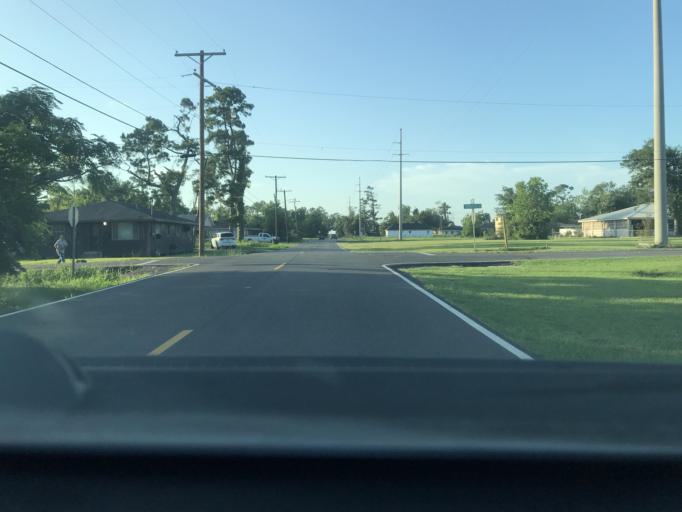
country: US
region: Louisiana
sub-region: Calcasieu Parish
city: Moss Bluff
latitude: 30.2586
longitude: -93.1954
